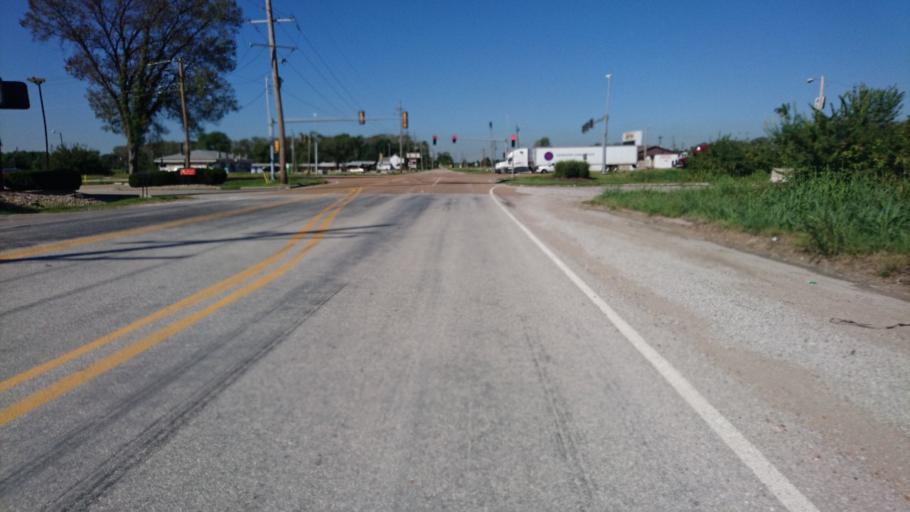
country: US
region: Illinois
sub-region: Madison County
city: Mitchell
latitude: 38.7621
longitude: -90.1234
